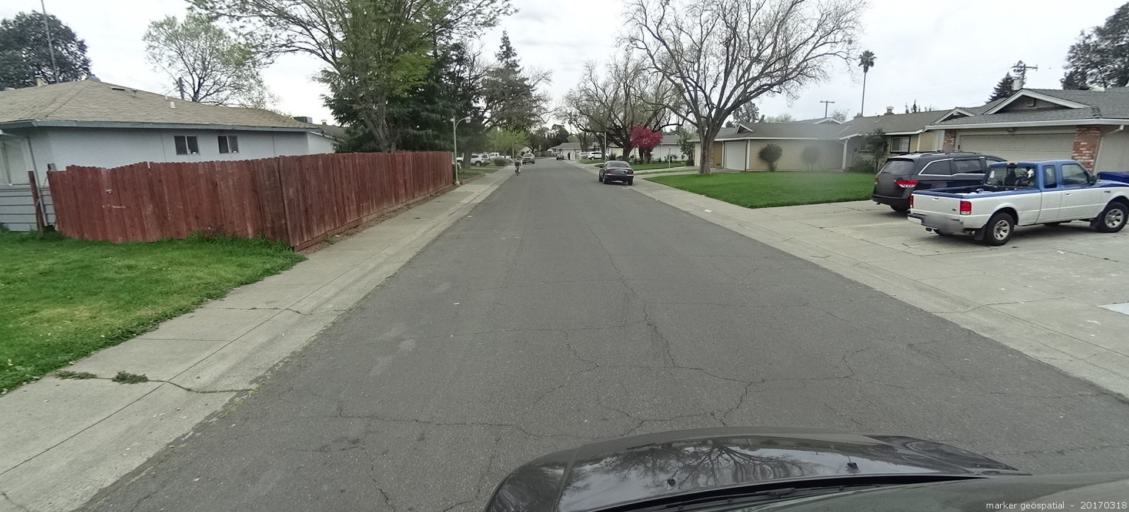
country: US
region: California
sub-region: Sacramento County
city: Parkway
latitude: 38.4848
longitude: -121.4507
